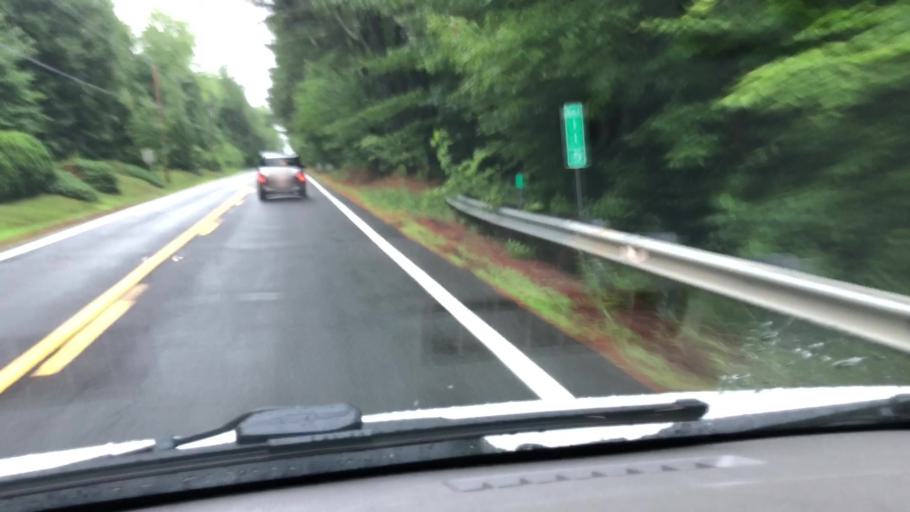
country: US
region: Massachusetts
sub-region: Hampshire County
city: Chesterfield
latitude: 42.3733
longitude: -72.9145
